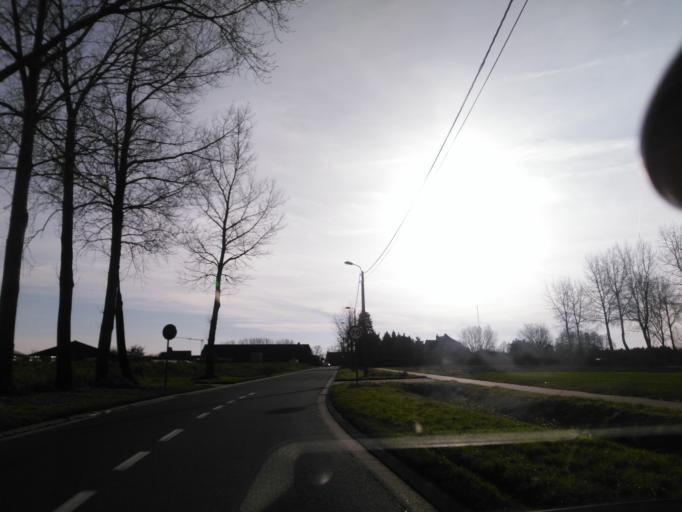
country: BE
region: Flanders
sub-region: Provincie Oost-Vlaanderen
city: Sint-Gillis-Waas
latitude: 51.2279
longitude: 4.1487
